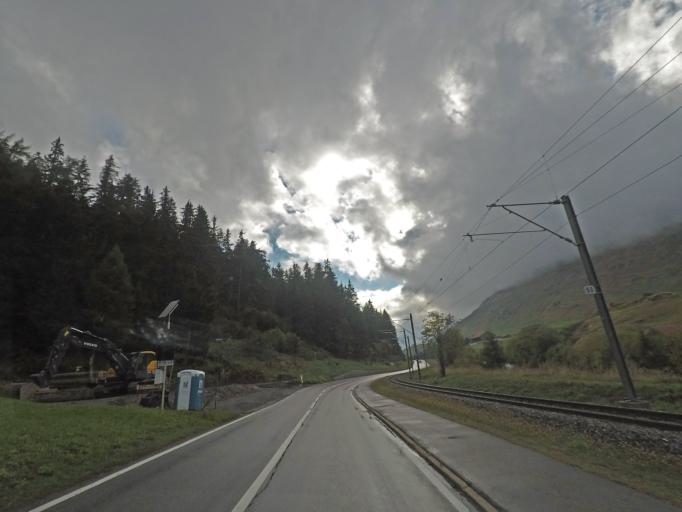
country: CH
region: Uri
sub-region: Uri
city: Andermatt
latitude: 46.6245
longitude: 8.5794
